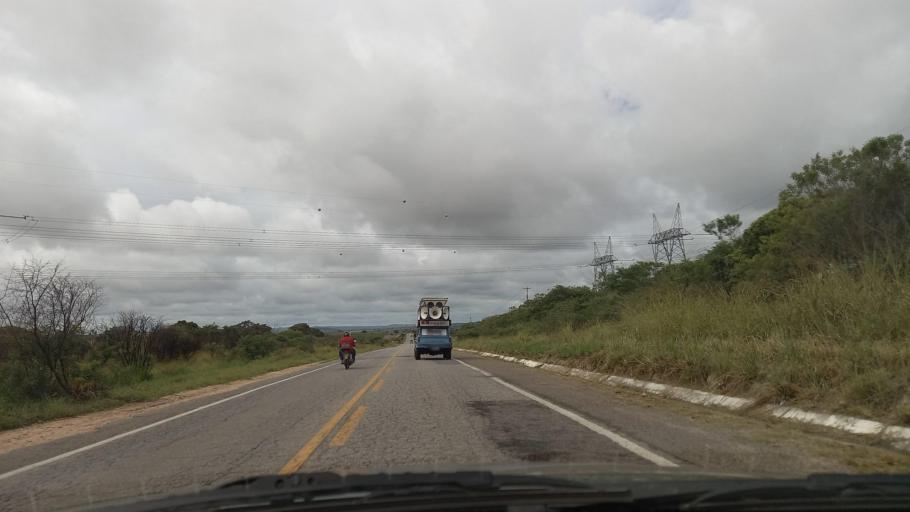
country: BR
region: Pernambuco
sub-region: Sao Joao
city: Sao Joao
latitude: -8.8797
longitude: -36.4015
